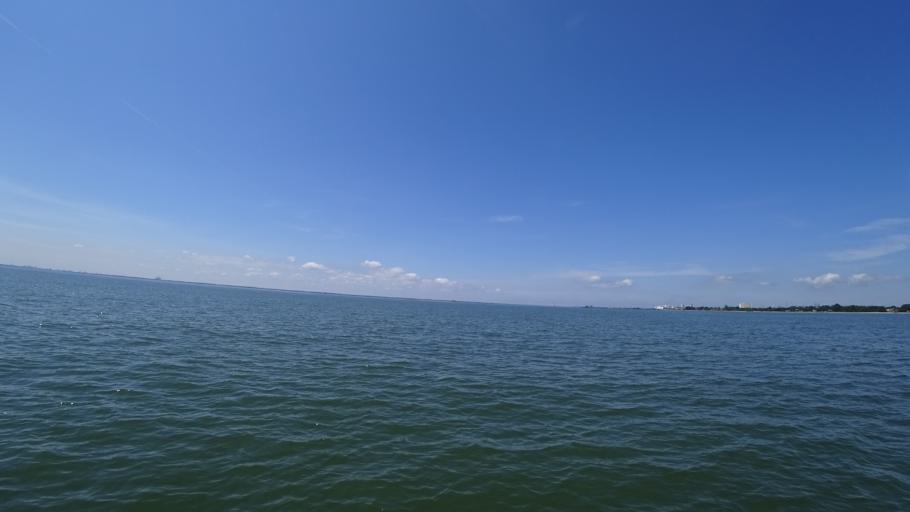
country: US
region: Virginia
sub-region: City of Newport News
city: Newport News
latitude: 36.9772
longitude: -76.3867
